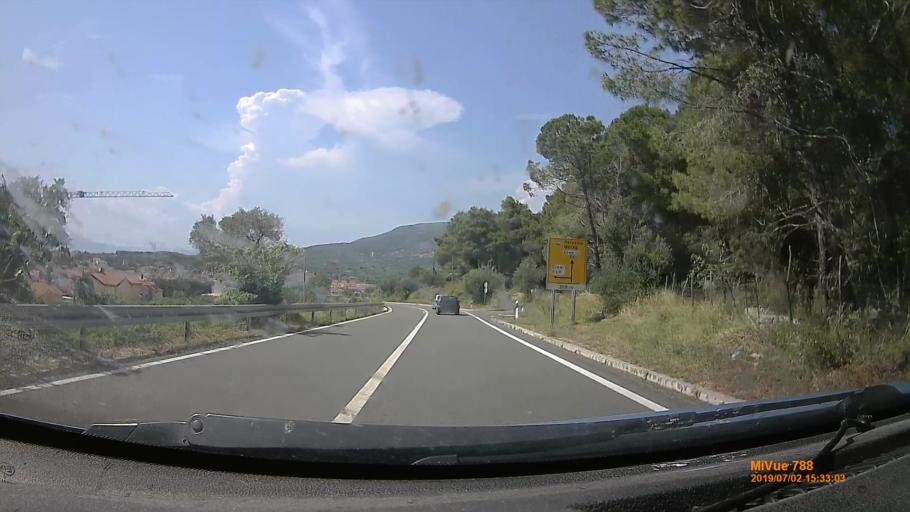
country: HR
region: Primorsko-Goranska
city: Cres
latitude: 44.9566
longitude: 14.4171
